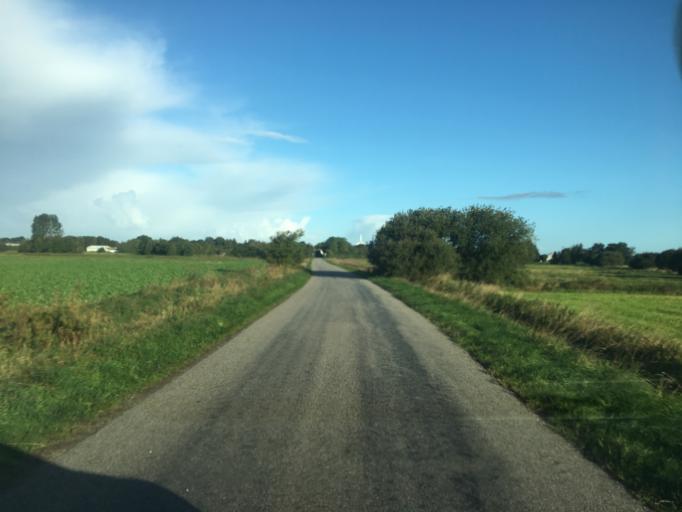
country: DE
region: Schleswig-Holstein
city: Ellhoft
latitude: 54.9574
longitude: 9.0165
